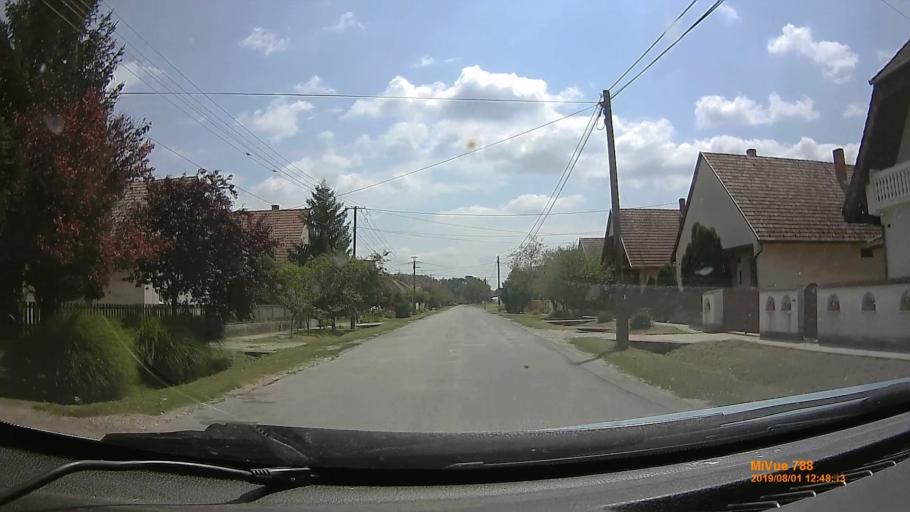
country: HR
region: Osjecko-Baranjska
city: Viljevo
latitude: 45.8200
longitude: 18.1051
